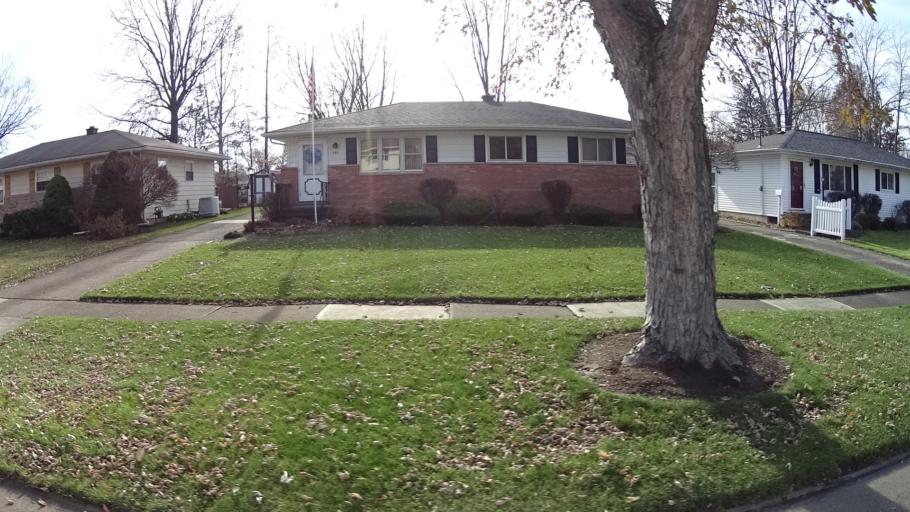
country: US
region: Ohio
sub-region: Lorain County
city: Sheffield
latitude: 41.4004
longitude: -82.0829
